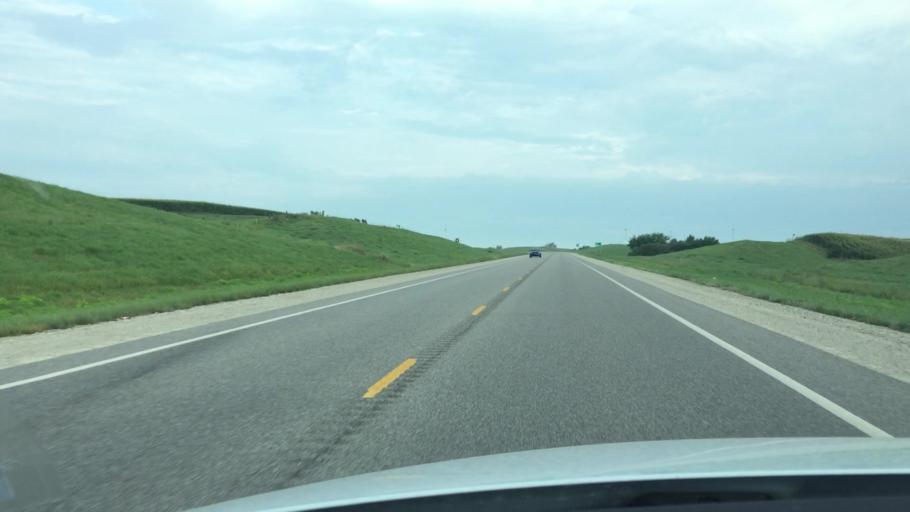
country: US
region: Kansas
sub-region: Doniphan County
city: Troy
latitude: 39.7967
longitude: -95.1093
